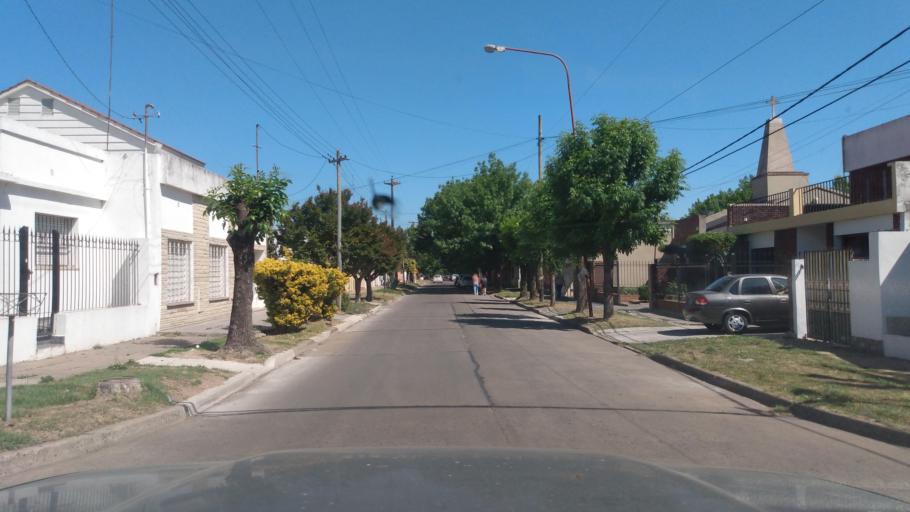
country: AR
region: Buenos Aires
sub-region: Partido de Lujan
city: Lujan
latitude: -34.5737
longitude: -59.1064
